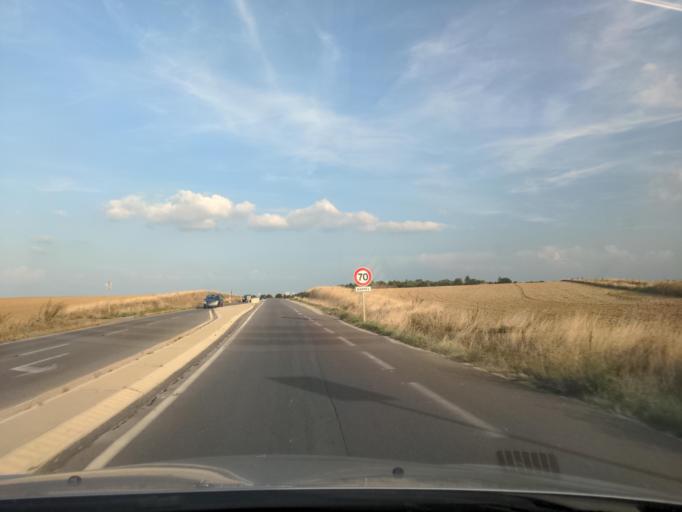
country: FR
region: Bourgogne
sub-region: Departement de la Cote-d'Or
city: Sennecey-les-Dijon
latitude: 47.2920
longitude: 5.0917
